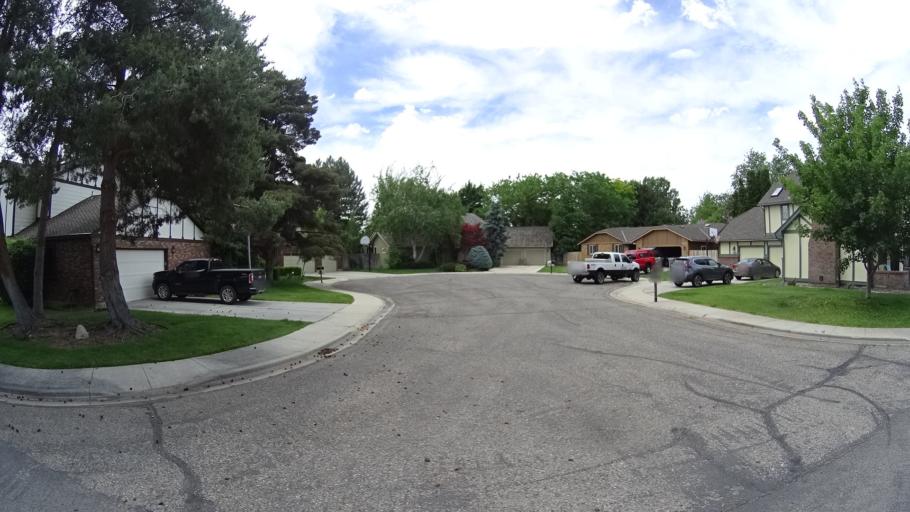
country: US
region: Idaho
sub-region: Ada County
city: Eagle
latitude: 43.6454
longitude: -116.3324
